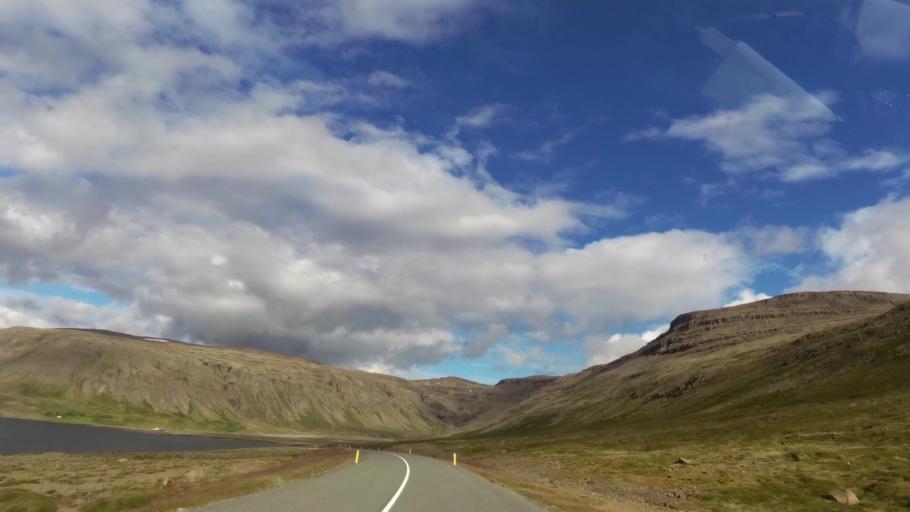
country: IS
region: West
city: Olafsvik
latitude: 65.5150
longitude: -23.8658
